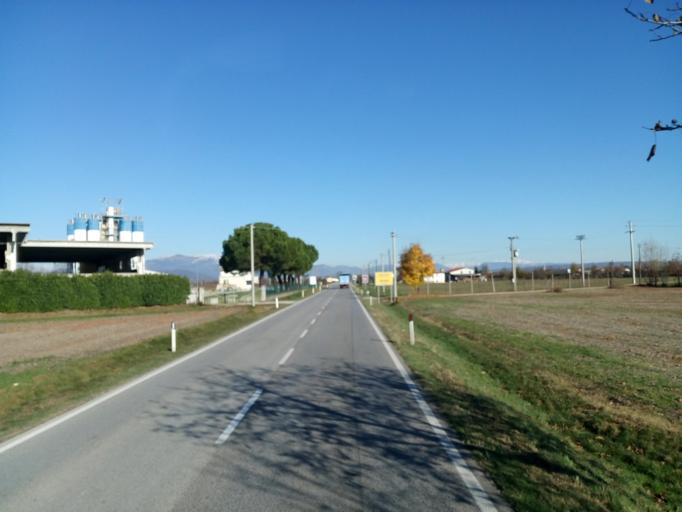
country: IT
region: Veneto
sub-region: Provincia di Treviso
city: Altivole
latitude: 45.7272
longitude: 11.9547
